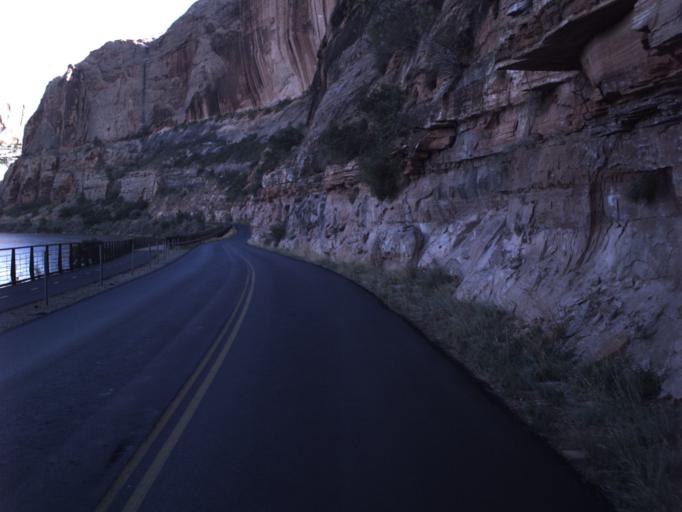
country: US
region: Utah
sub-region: Grand County
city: Moab
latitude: 38.6102
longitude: -109.5497
